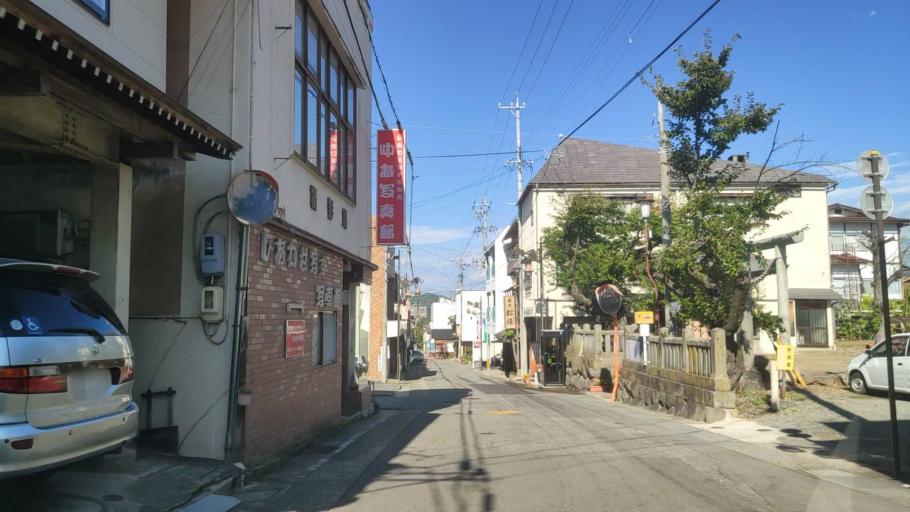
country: JP
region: Nagano
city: Nakano
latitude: 36.7409
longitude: 138.4175
